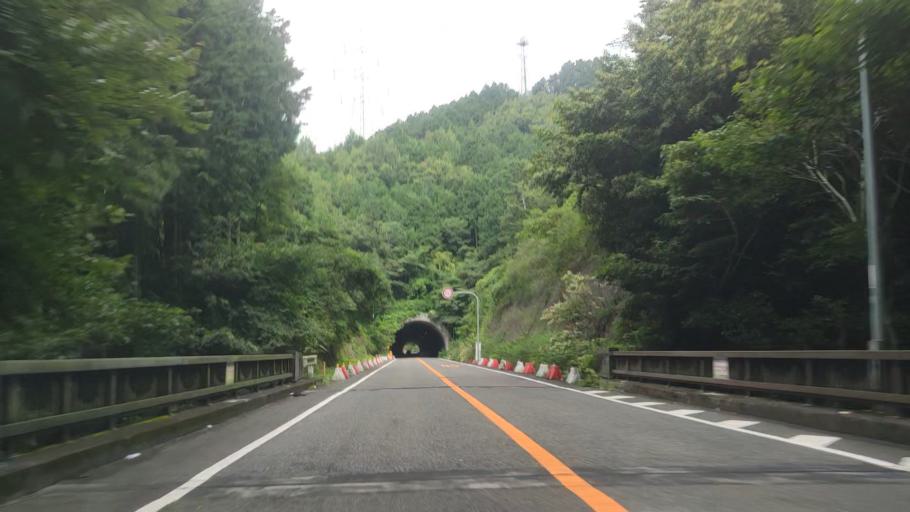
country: JP
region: Osaka
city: Tondabayashicho
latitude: 34.4186
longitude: 135.5866
